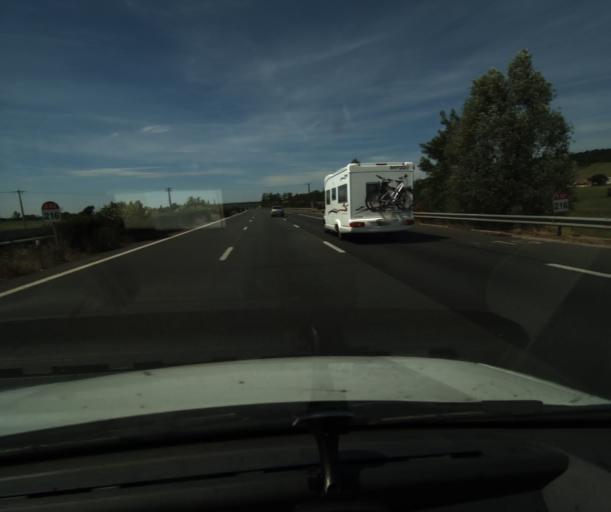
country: FR
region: Midi-Pyrenees
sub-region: Departement de la Haute-Garonne
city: Bruguieres
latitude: 43.7319
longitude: 1.3972
